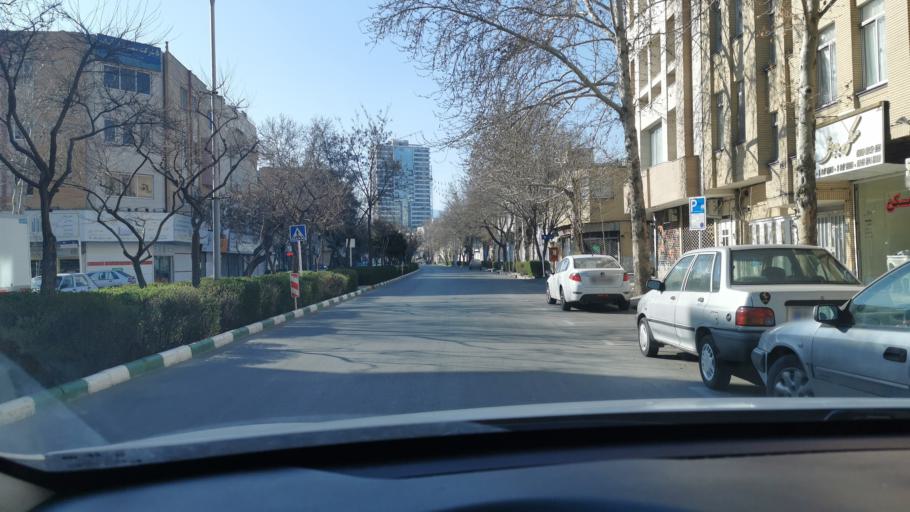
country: IR
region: Razavi Khorasan
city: Mashhad
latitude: 36.2889
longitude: 59.5673
